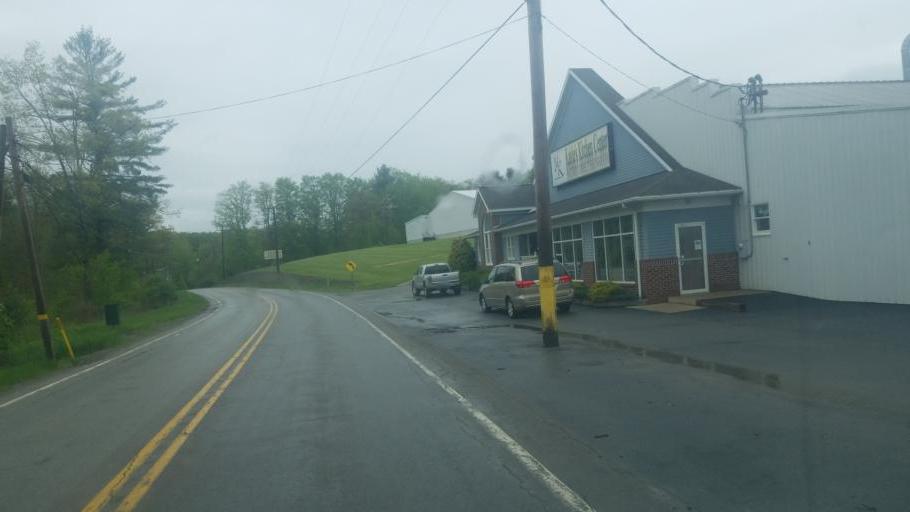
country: US
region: Pennsylvania
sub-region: Clarion County
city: Marianne
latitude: 41.3777
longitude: -79.3123
